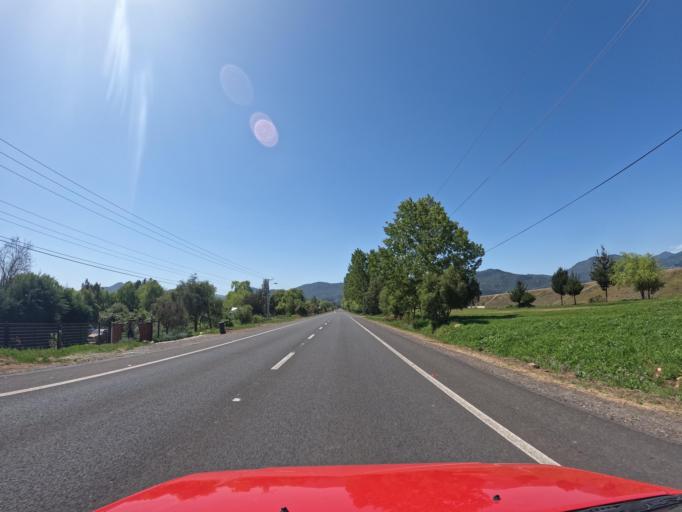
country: CL
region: Maule
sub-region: Provincia de Linares
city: Colbun
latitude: -35.7126
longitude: -71.3996
